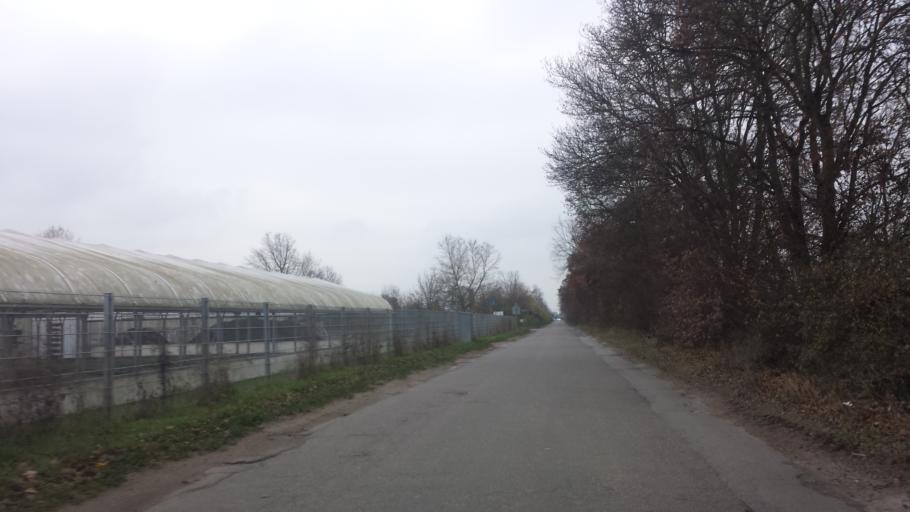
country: DE
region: Hesse
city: Lampertheim
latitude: 49.6227
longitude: 8.4791
